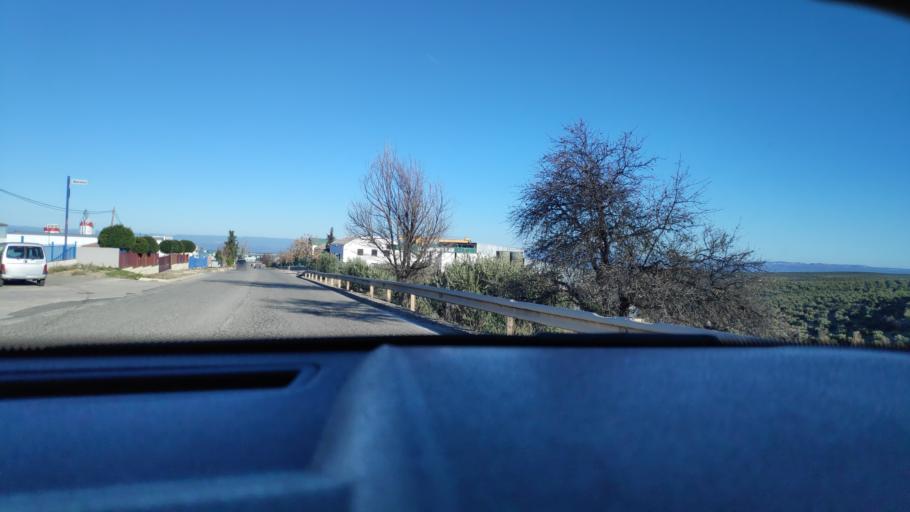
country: ES
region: Andalusia
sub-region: Provincia de Jaen
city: Mancha Real
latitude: 37.8004
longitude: -3.6098
